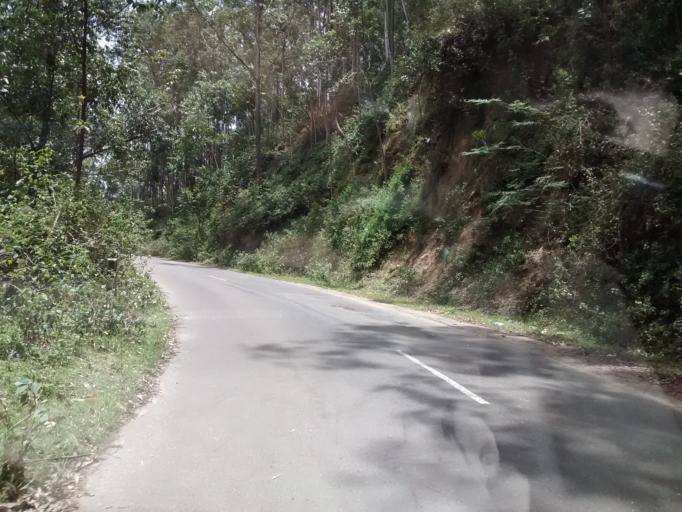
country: IN
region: Kerala
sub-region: Idukki
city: Munnar
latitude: 10.1364
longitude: 77.1844
